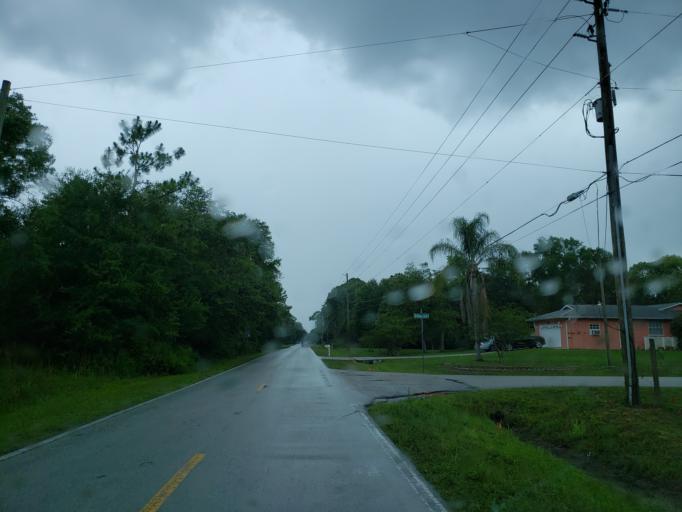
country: US
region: Florida
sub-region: Pasco County
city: Wesley Chapel
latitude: 28.2627
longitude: -82.3717
